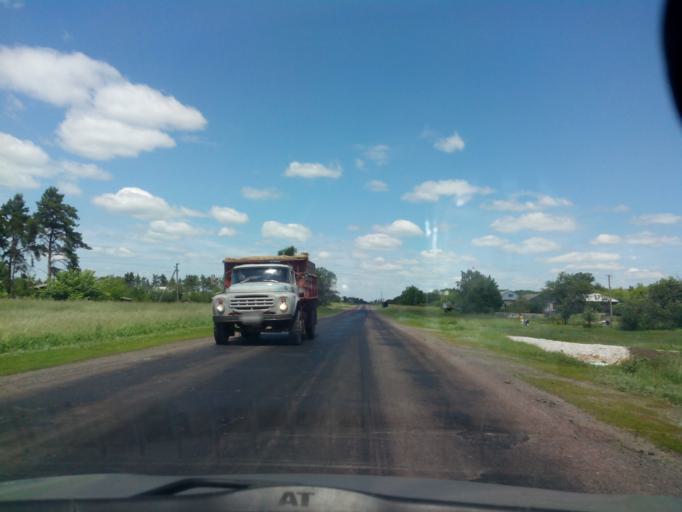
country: RU
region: Tambov
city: Zherdevka
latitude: 51.7846
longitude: 41.5099
